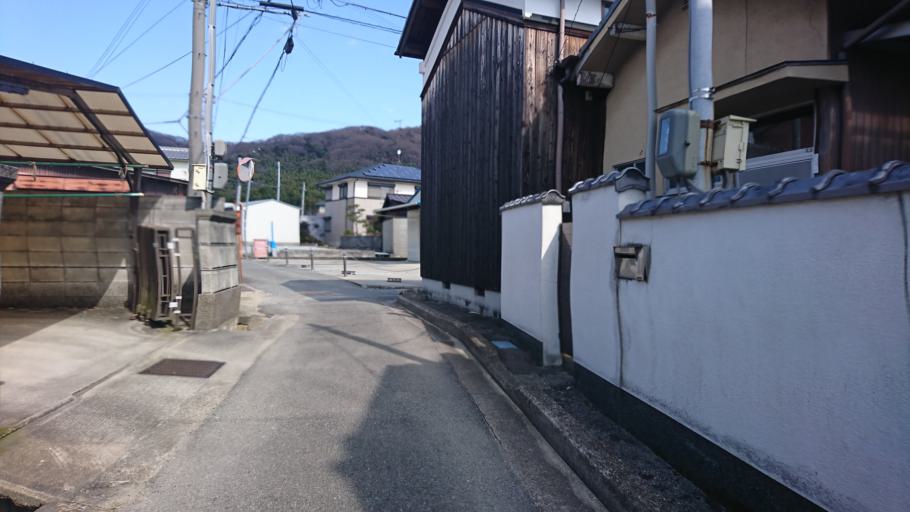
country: JP
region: Hyogo
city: Kakogawacho-honmachi
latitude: 34.8255
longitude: 134.8033
